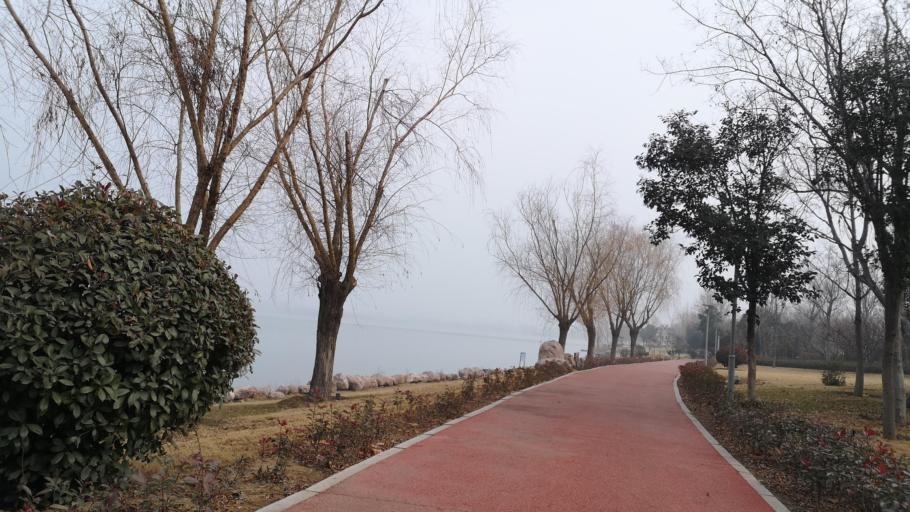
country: CN
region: Henan Sheng
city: Zhongyuanlu
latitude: 35.8004
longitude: 115.0473
